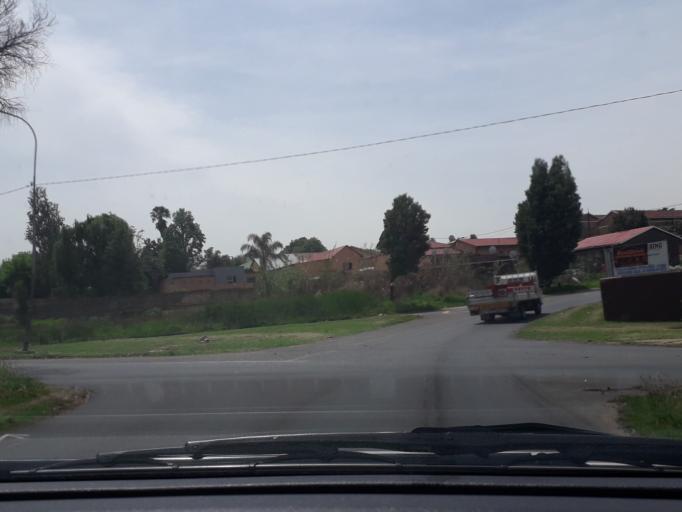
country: ZA
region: Gauteng
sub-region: City of Johannesburg Metropolitan Municipality
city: Roodepoort
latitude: -26.1795
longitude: 27.9352
